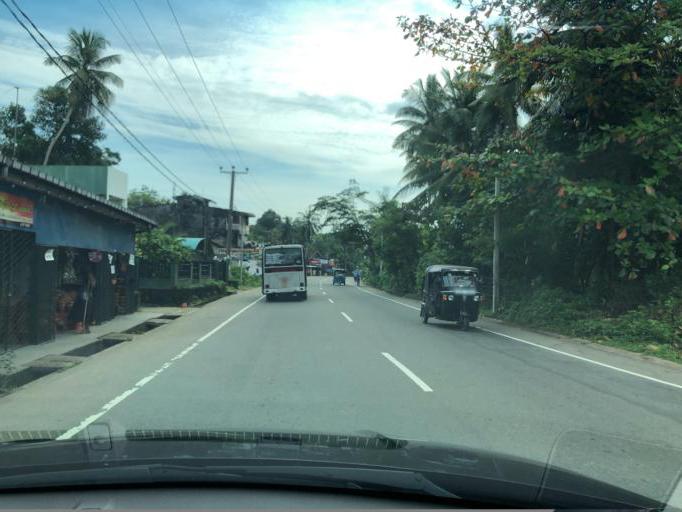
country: LK
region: Western
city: Kalutara
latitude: 6.5536
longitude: 80.0203
